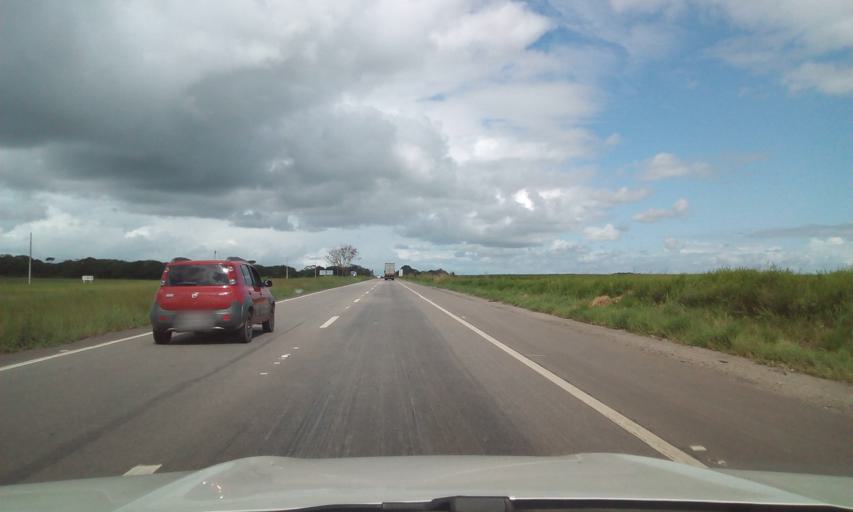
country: BR
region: Pernambuco
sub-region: Goiana
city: Goiana
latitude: -7.6339
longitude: -34.9612
